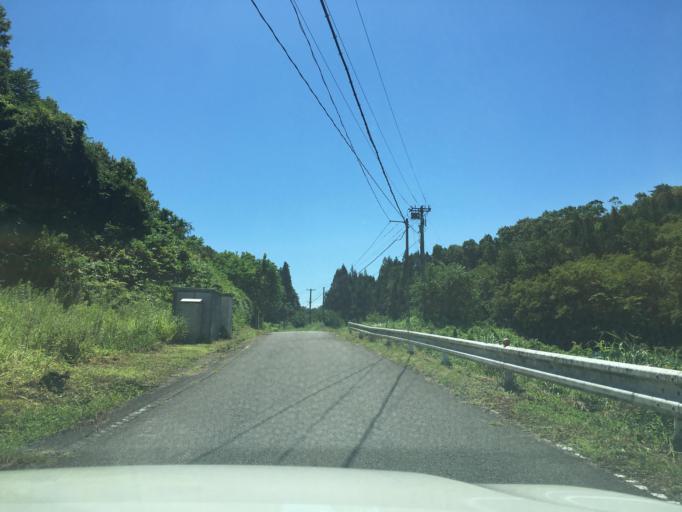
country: JP
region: Fukushima
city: Ishikawa
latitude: 37.2206
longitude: 140.5215
